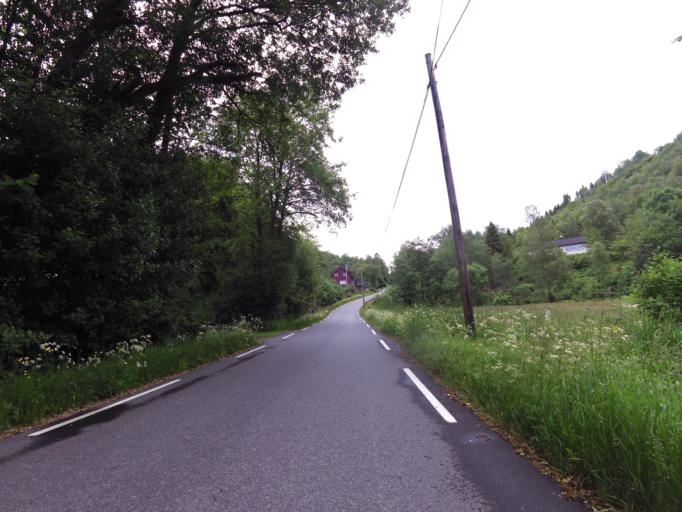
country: NO
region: Vest-Agder
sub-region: Lyngdal
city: Lyngdal
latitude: 58.1109
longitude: 6.9566
